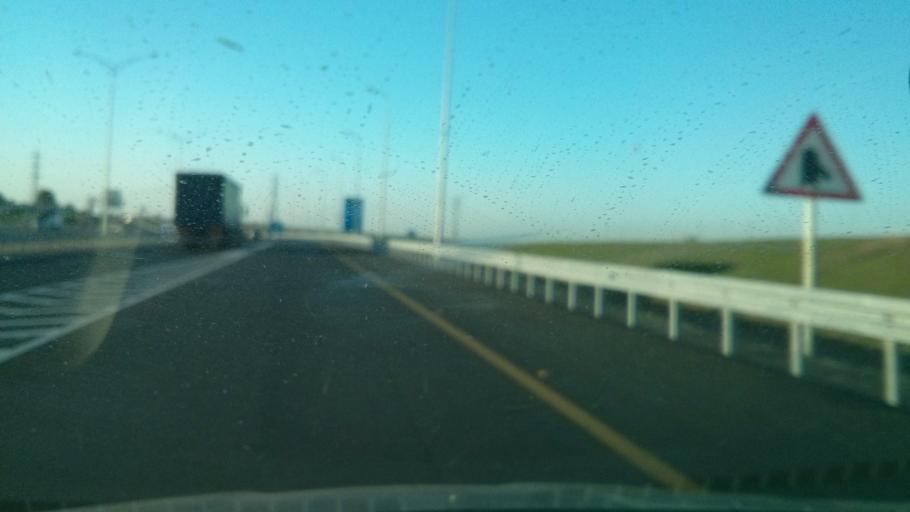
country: IL
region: Southern District
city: Lehavim
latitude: 31.4262
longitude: 34.7839
